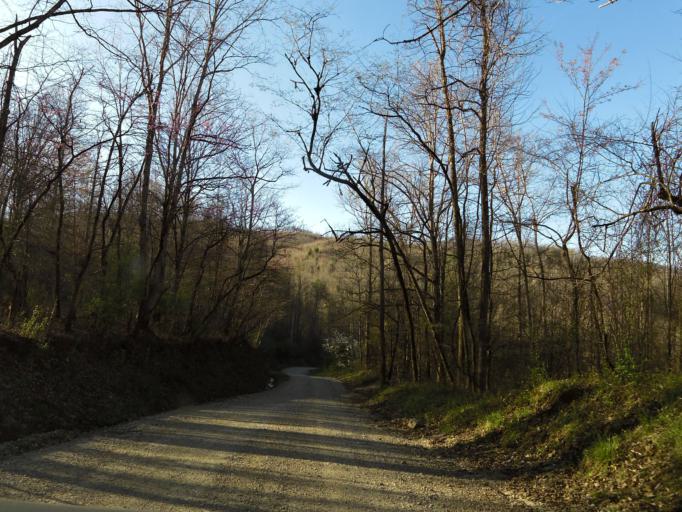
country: US
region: Tennessee
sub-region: Campbell County
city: Caryville
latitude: 36.2566
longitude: -84.3955
